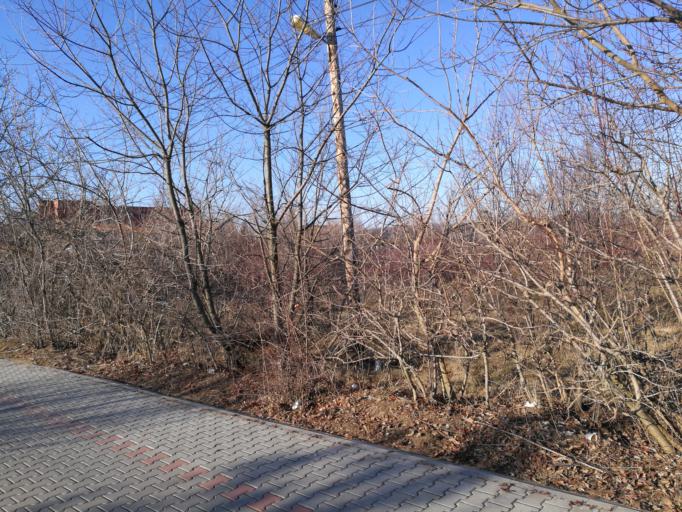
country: RO
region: Ilfov
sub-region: Comuna Otopeni
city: Otopeni
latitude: 44.5071
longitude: 26.0773
